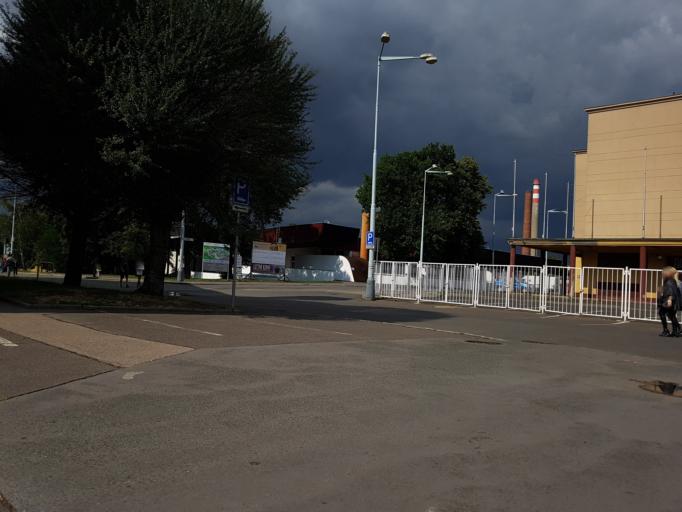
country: CZ
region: Praha
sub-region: Praha 8
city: Karlin
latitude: 50.1067
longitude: 14.4315
